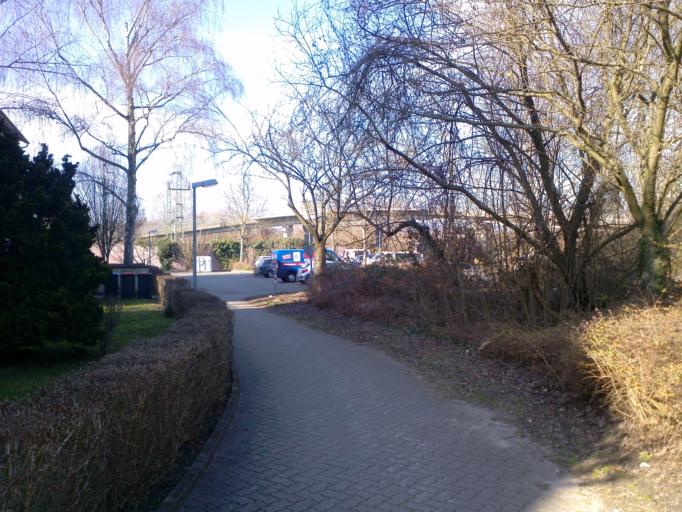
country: DE
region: Baden-Wuerttemberg
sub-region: Karlsruhe Region
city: Karlsruhe
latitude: 48.9874
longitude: 8.3942
